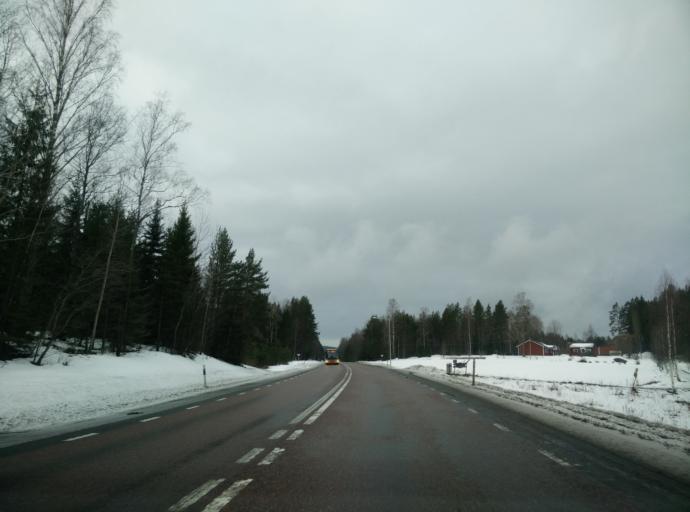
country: SE
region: Gaevleborg
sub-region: Hofors Kommun
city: Hofors
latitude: 60.5699
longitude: 16.4110
